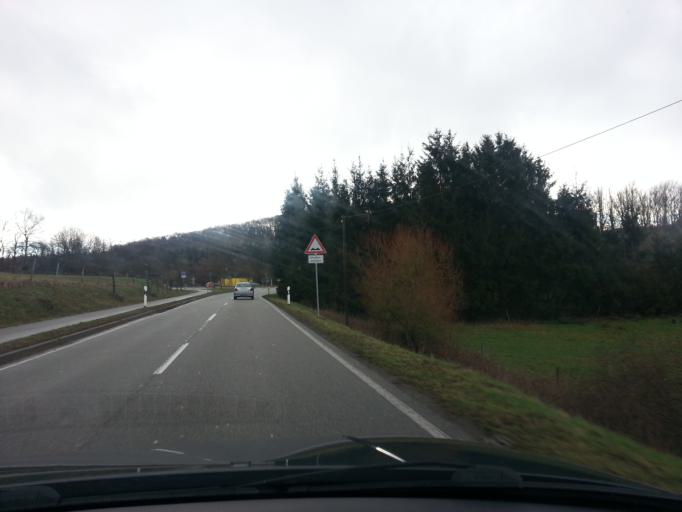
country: DE
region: Rheinland-Pfalz
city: Reichenbach-Steegen
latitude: 49.4974
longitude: 7.5500
